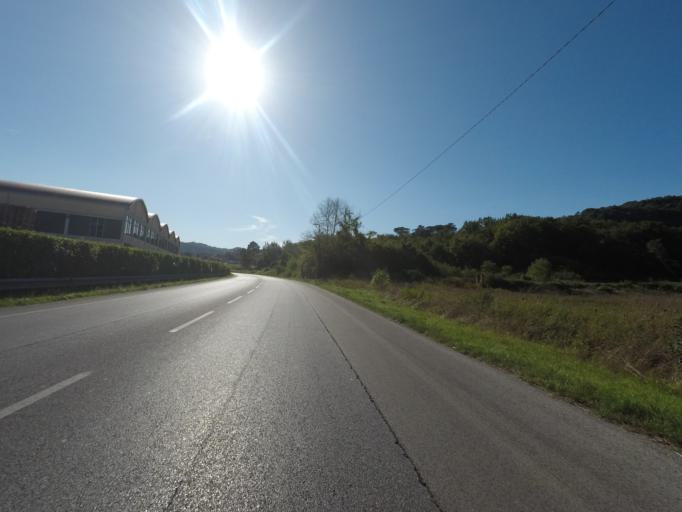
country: IT
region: Tuscany
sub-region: Provincia di Lucca
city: San Martino in Freddana-Monsagrati
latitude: 43.9089
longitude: 10.4264
